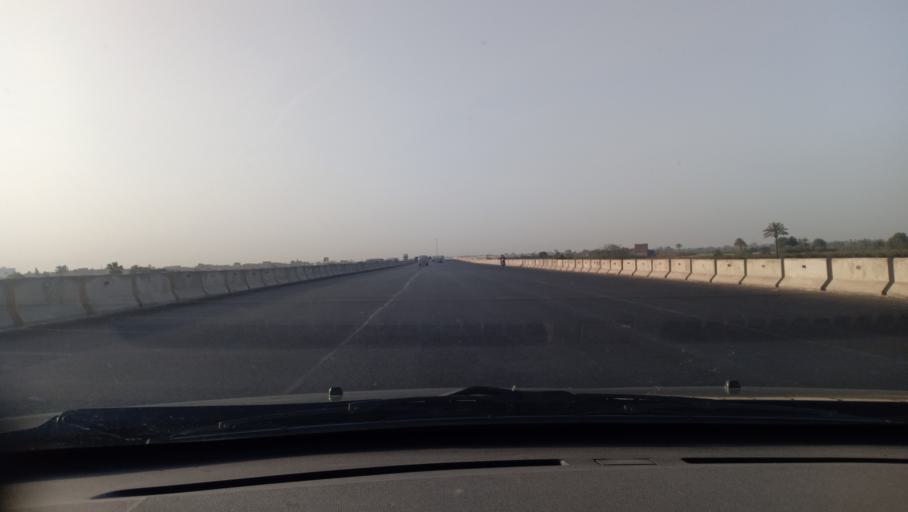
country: EG
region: Muhafazat al Qalyubiyah
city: Qalyub
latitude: 30.1859
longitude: 31.2415
